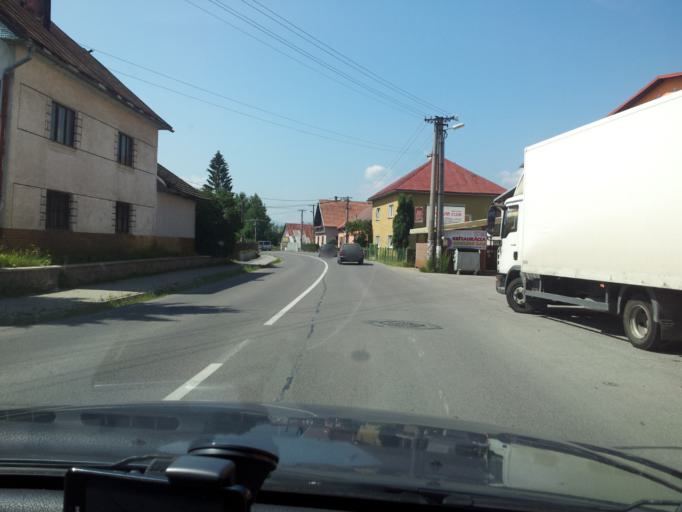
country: SK
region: Zilinsky
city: Namestovo
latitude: 49.3658
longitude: 19.4095
